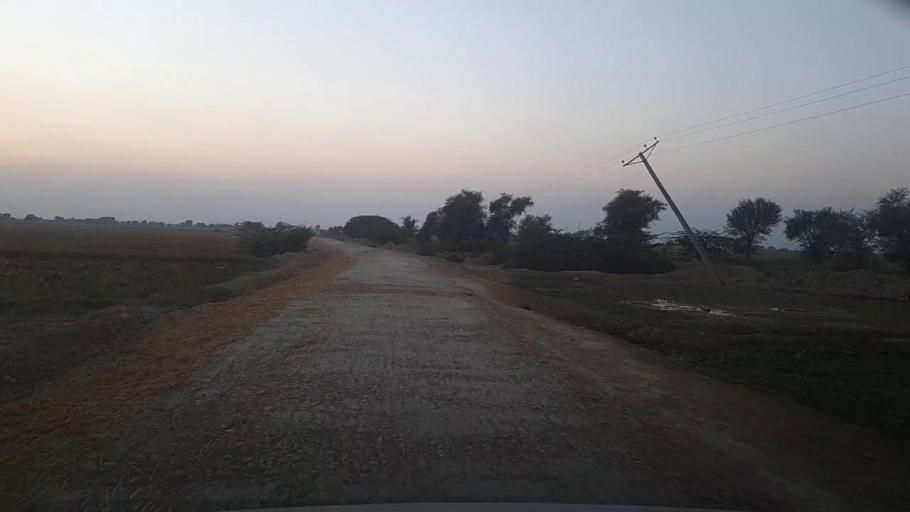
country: PK
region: Sindh
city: Khairpur Nathan Shah
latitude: 27.1813
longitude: 67.6066
